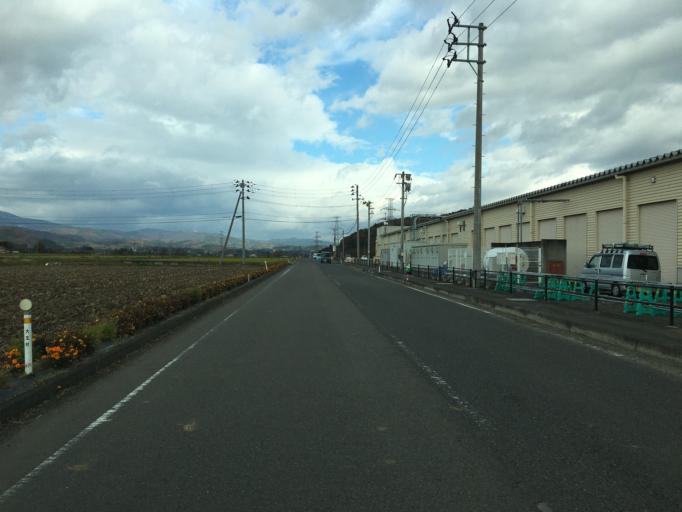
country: JP
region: Fukushima
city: Motomiya
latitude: 37.5414
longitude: 140.3947
